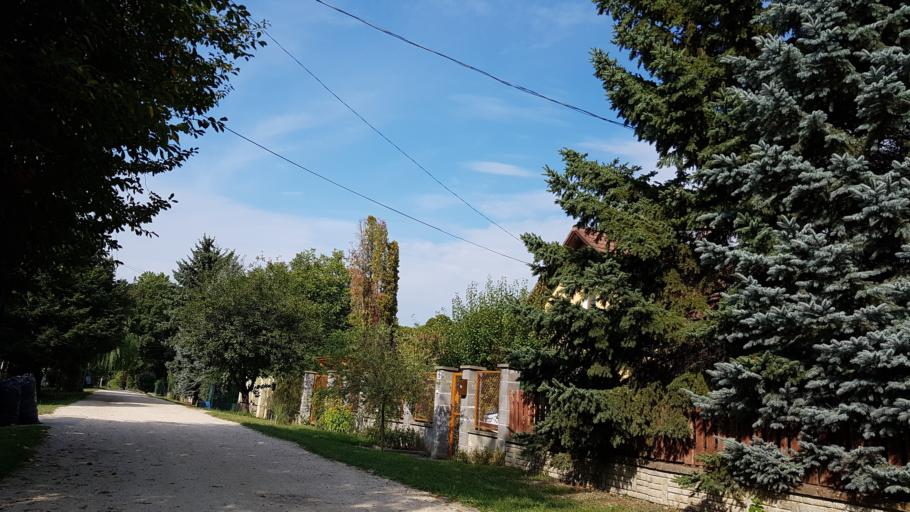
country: HU
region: Fejer
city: Gardony
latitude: 47.1948
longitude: 18.6079
